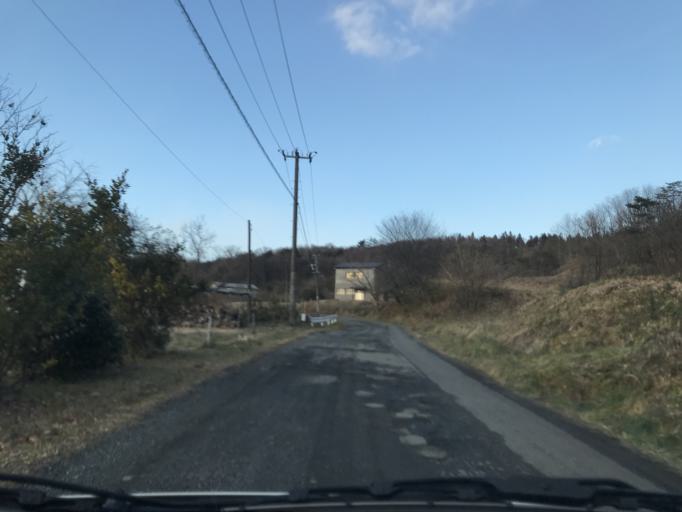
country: JP
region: Iwate
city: Mizusawa
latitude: 39.0309
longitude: 141.1039
